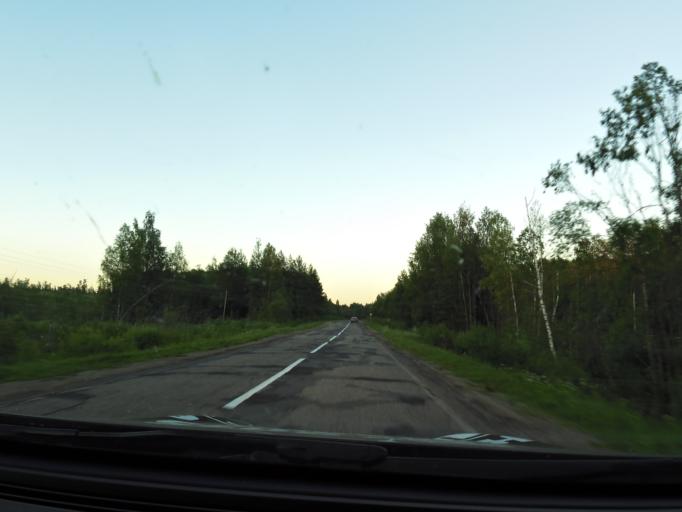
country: RU
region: Jaroslavl
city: Lyubim
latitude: 58.3420
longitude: 40.8337
